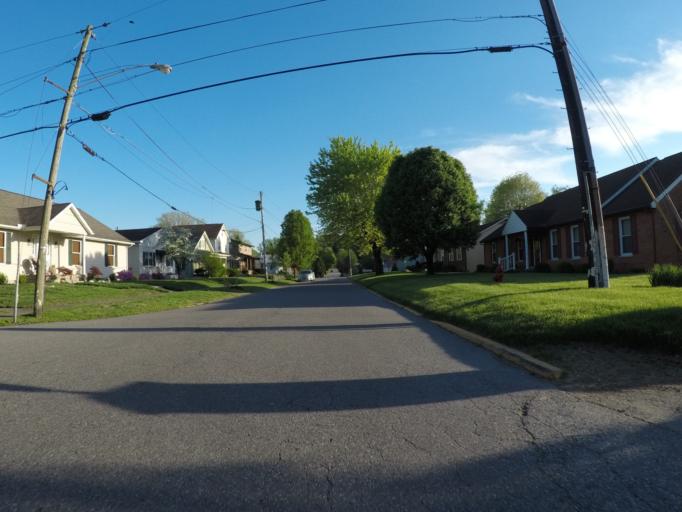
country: US
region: West Virginia
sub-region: Wayne County
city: Ceredo
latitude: 38.3957
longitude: -82.5600
